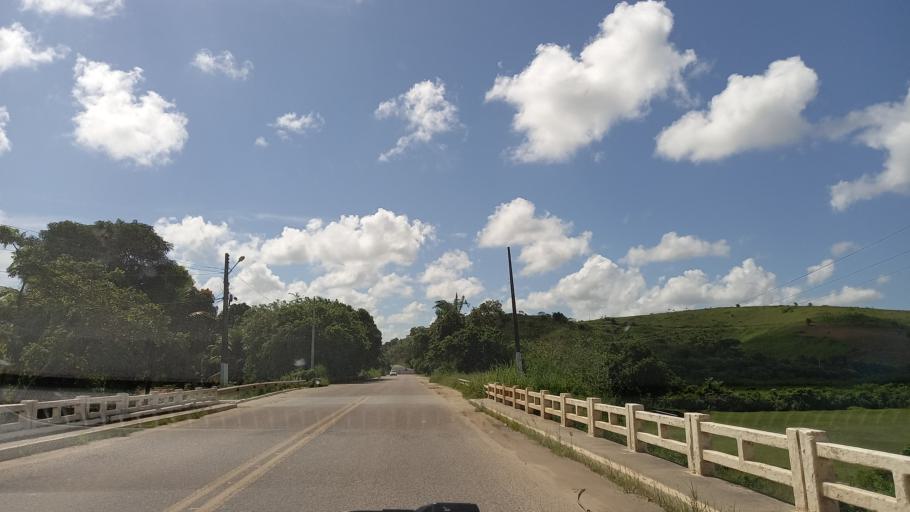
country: BR
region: Pernambuco
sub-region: Barreiros
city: Barreiros
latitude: -8.8117
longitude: -35.1832
